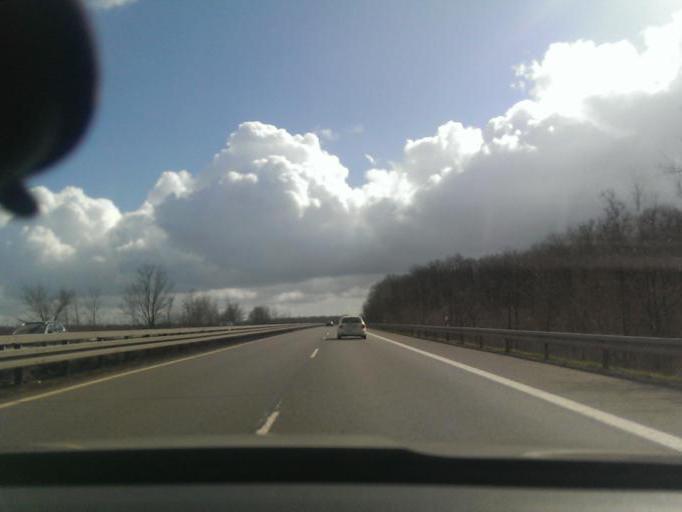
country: DE
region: Lower Saxony
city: Lehre
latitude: 52.3473
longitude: 10.7298
